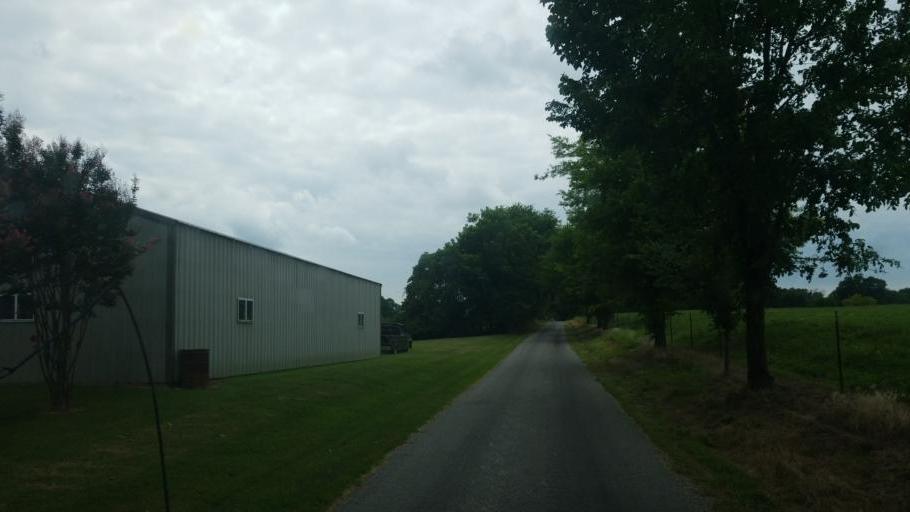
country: US
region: Illinois
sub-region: Jackson County
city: Murphysboro
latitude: 37.7034
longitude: -89.3437
